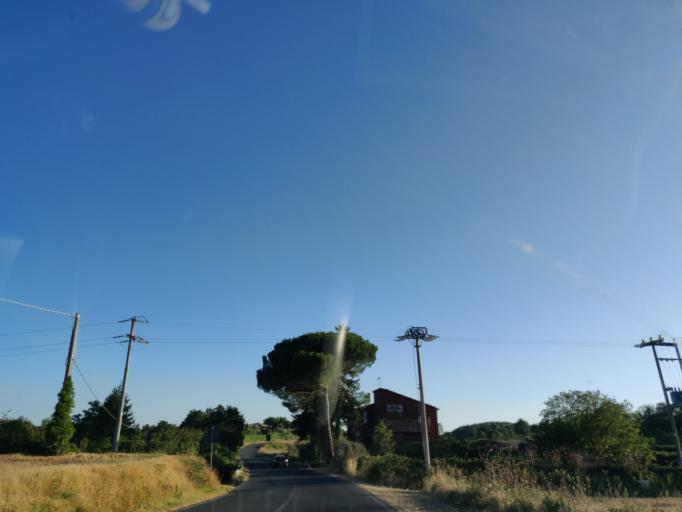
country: IT
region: Latium
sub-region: Provincia di Viterbo
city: Gradoli
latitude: 42.6628
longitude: 11.8527
